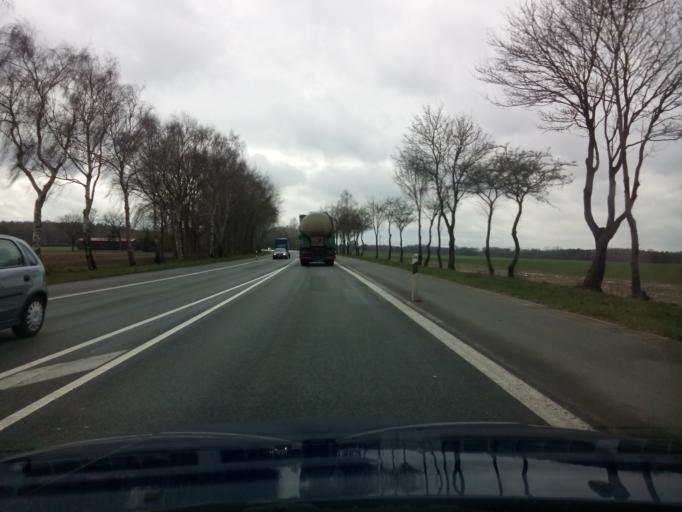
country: DE
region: Lower Saxony
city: Wildeshausen
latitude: 52.9264
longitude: 8.4631
